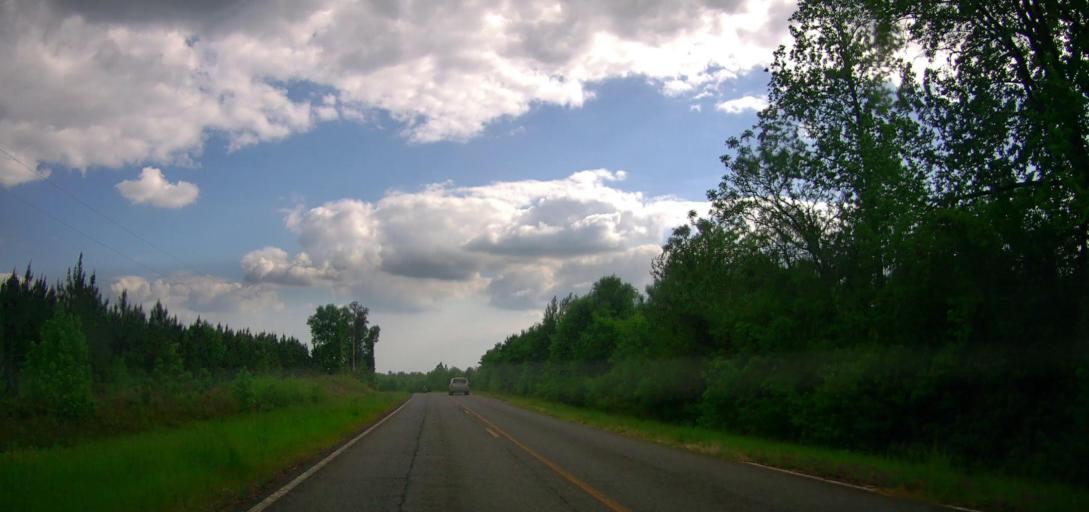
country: US
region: Georgia
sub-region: Washington County
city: Tennille
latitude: 32.7668
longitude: -82.9303
